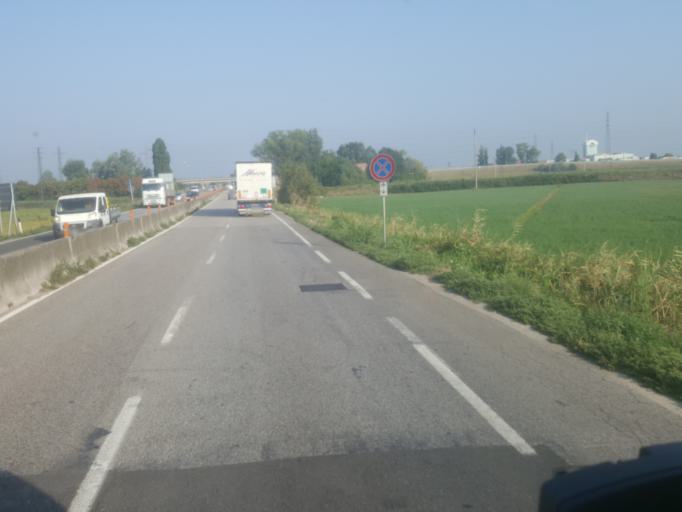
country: IT
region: Emilia-Romagna
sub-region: Provincia di Ravenna
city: Fornace Zarattini
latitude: 44.4249
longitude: 12.1590
